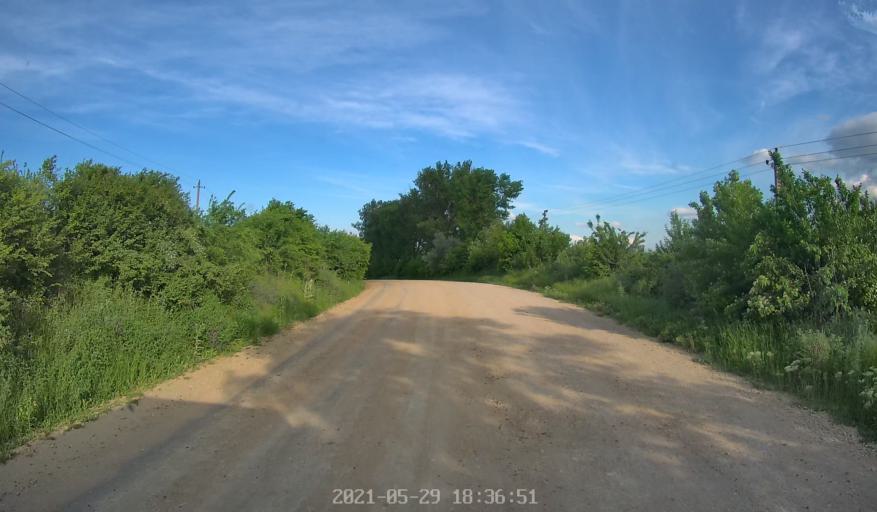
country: MD
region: Chisinau
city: Singera
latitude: 46.8054
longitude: 28.9269
